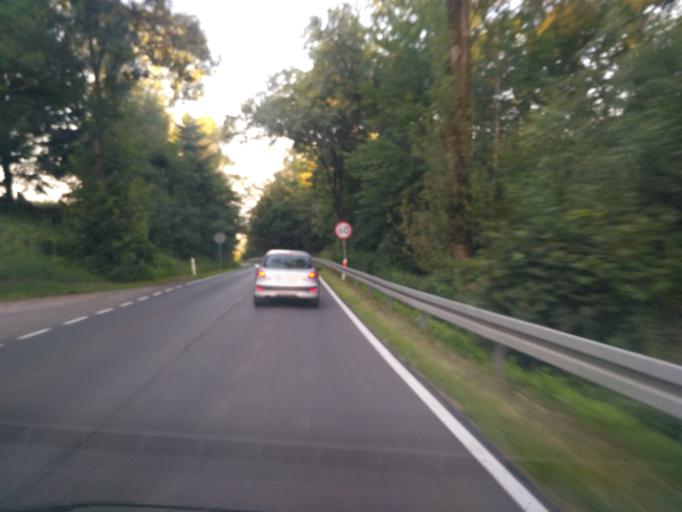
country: PL
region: Subcarpathian Voivodeship
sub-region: Powiat krosnienski
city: Korczyna
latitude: 49.7372
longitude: 21.8069
